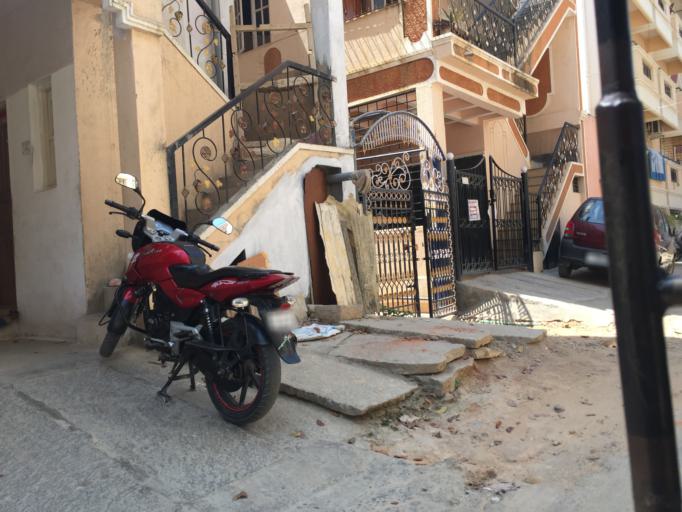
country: IN
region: Karnataka
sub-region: Bangalore Urban
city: Bangalore
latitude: 13.0061
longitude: 77.6234
